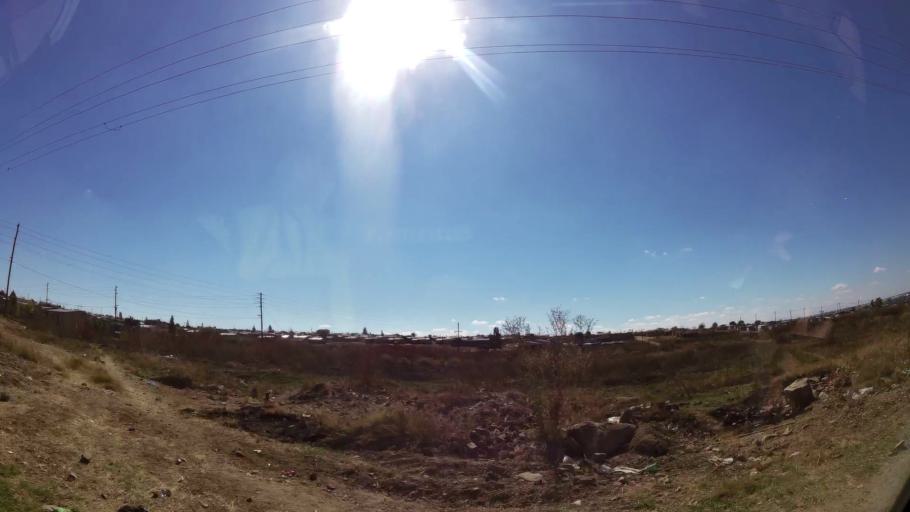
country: ZA
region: Limpopo
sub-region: Capricorn District Municipality
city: Polokwane
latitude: -23.8868
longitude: 29.4118
